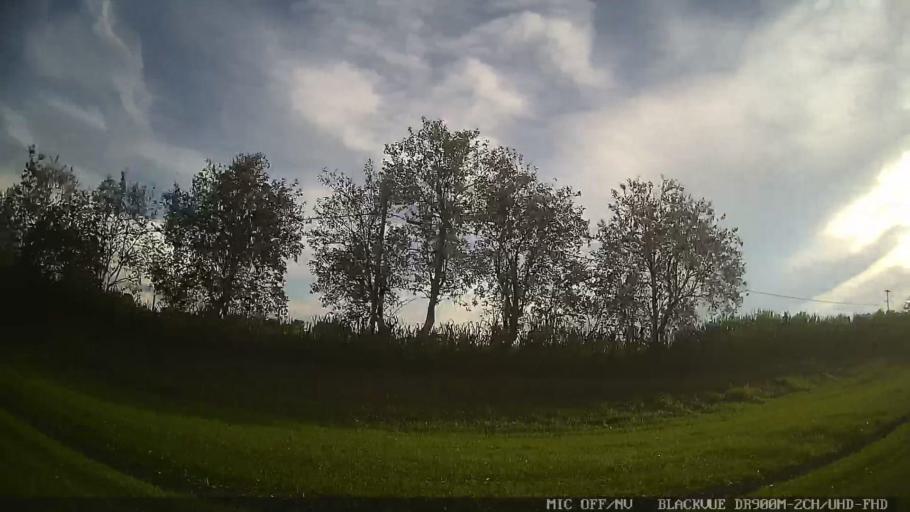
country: BR
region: Sao Paulo
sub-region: Tiete
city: Tiete
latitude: -23.1425
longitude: -47.6739
